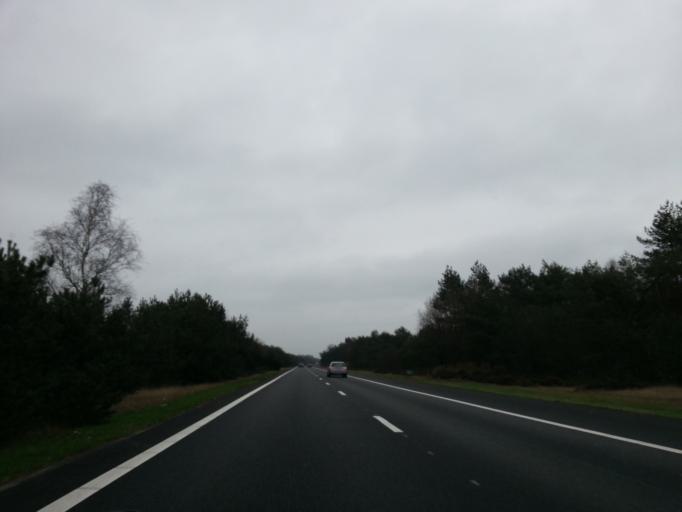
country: NL
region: Gelderland
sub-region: Gemeente Oldebroek
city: Oldebroek
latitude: 52.4179
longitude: 5.9093
